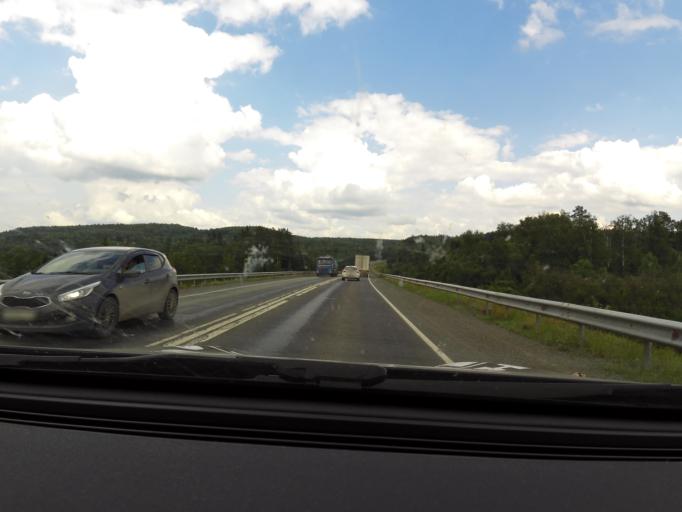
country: RU
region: Sverdlovsk
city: Bisert'
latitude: 56.8376
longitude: 58.8604
